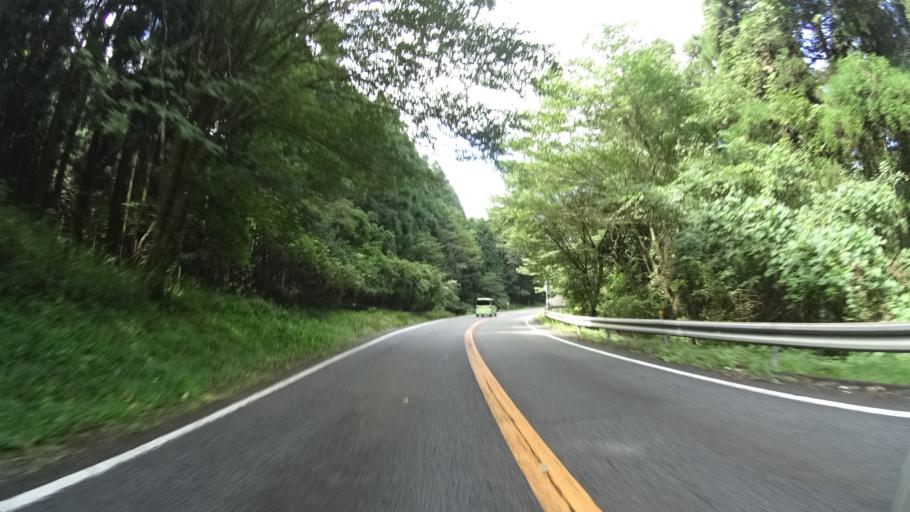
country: JP
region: Oita
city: Tsukawaki
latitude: 33.1966
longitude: 131.2529
